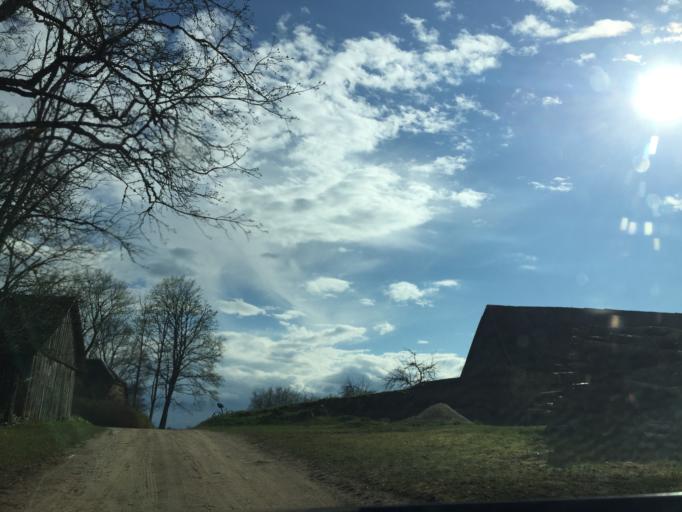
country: LV
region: Aluksnes Rajons
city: Aluksne
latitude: 57.4308
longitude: 26.9719
